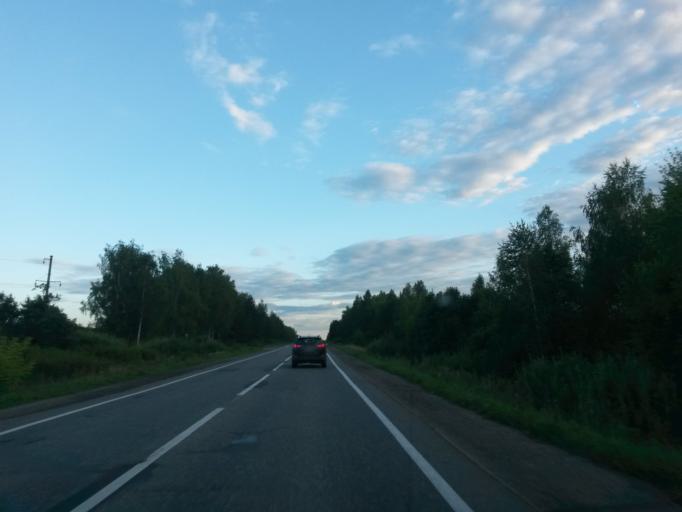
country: RU
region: Jaroslavl
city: Gavrilov-Yam
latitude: 57.3666
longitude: 39.9078
